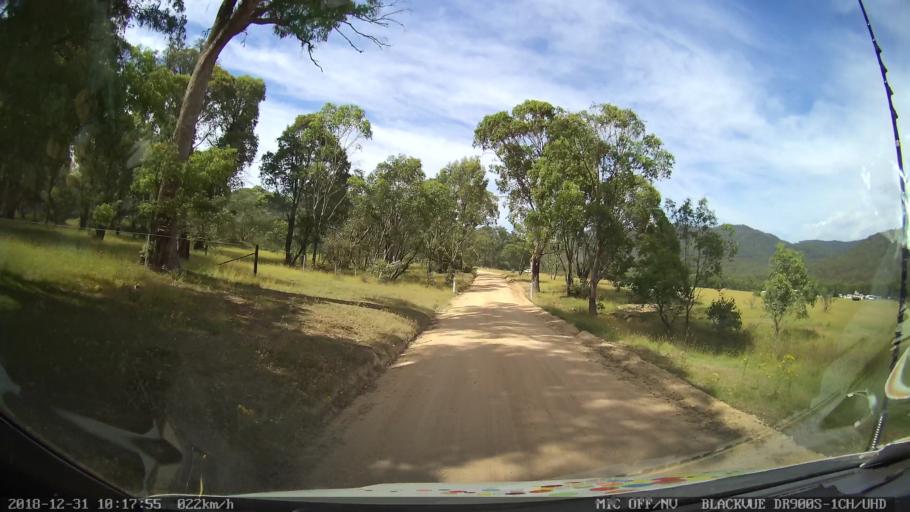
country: AU
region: New South Wales
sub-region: Snowy River
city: Jindabyne
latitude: -36.5417
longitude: 148.1343
